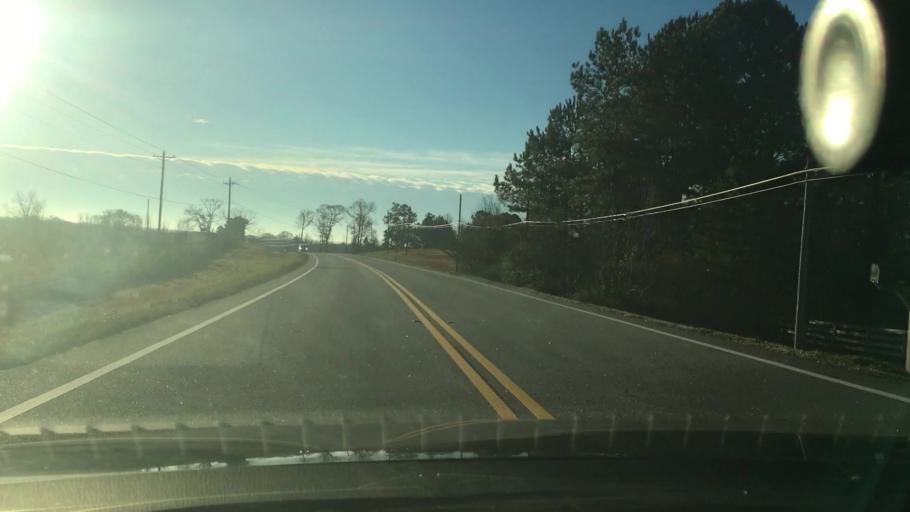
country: US
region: Georgia
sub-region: Coweta County
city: Senoia
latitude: 33.2774
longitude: -84.5338
